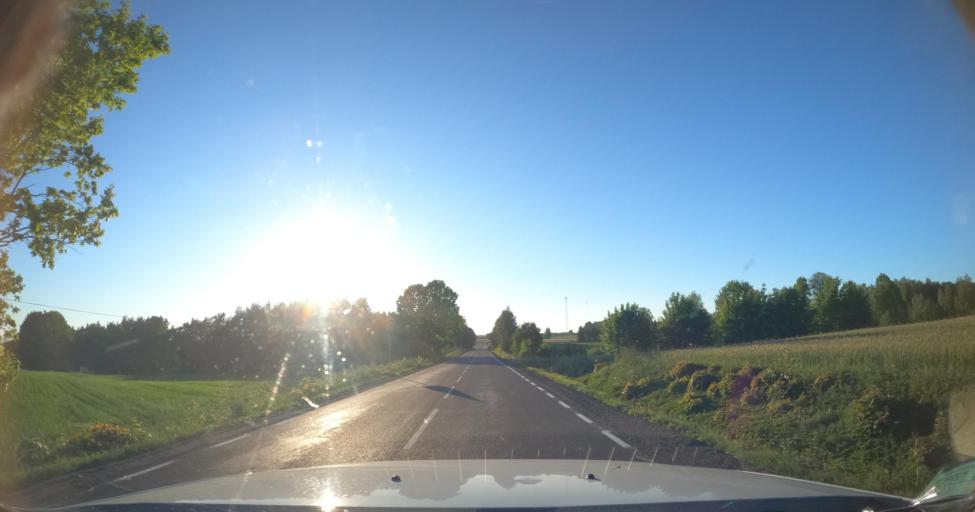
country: PL
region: Pomeranian Voivodeship
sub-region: Powiat bytowski
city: Czarna Dabrowka
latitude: 54.3500
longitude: 17.5802
